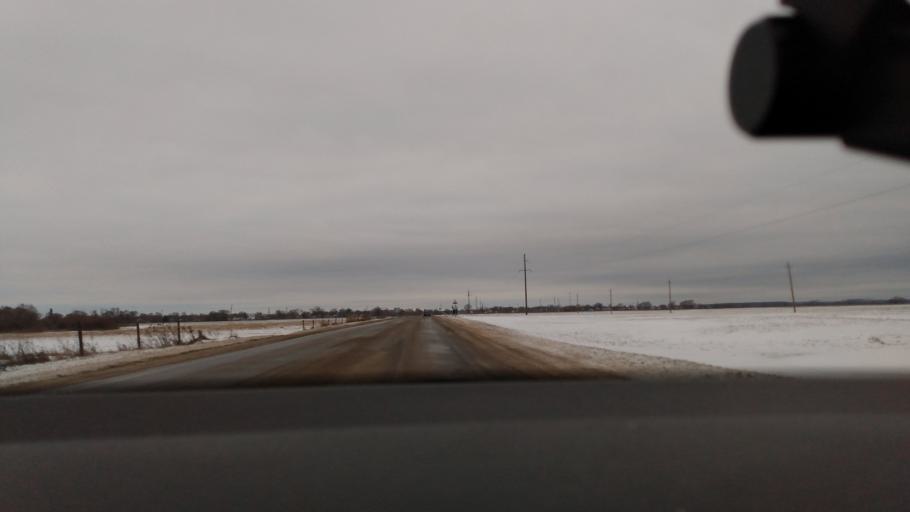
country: RU
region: Moskovskaya
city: Krasnaya Poyma
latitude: 55.0699
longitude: 39.1261
